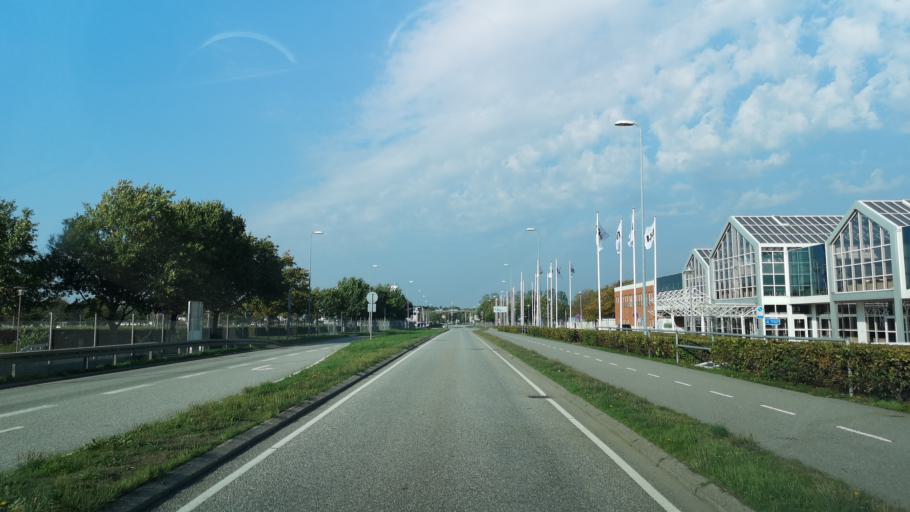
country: DK
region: Central Jutland
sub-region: Herning Kommune
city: Herning
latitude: 56.1213
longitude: 8.9489
